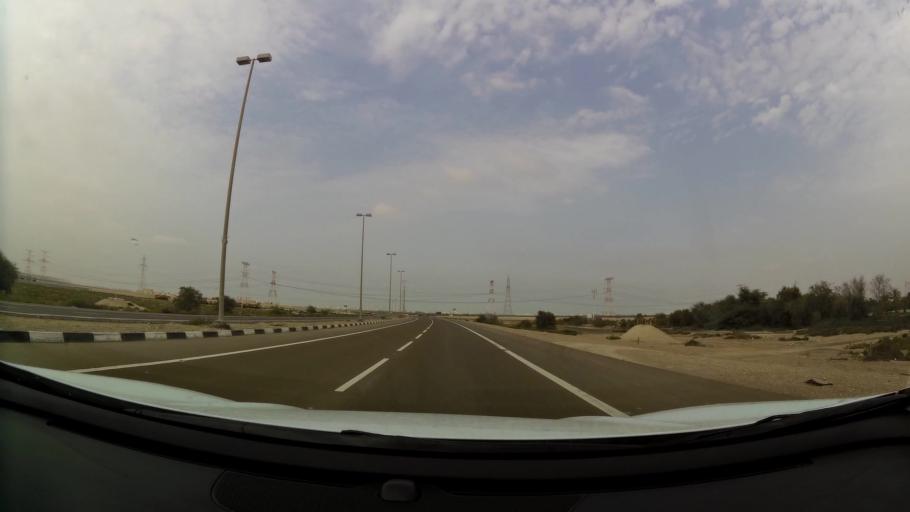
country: AE
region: Abu Dhabi
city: Abu Dhabi
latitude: 24.6325
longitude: 54.7016
